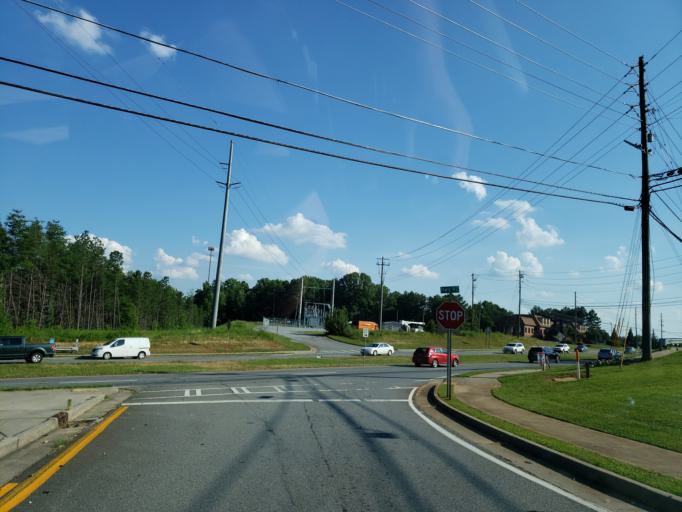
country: US
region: Georgia
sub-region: Cherokee County
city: Woodstock
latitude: 34.0874
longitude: -84.5494
